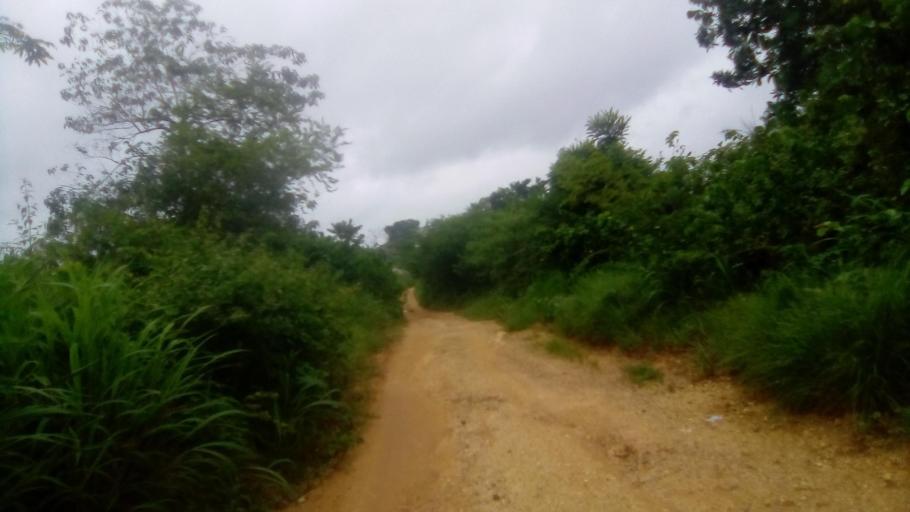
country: SL
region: Eastern Province
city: Kailahun
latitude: 8.2982
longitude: -10.5571
